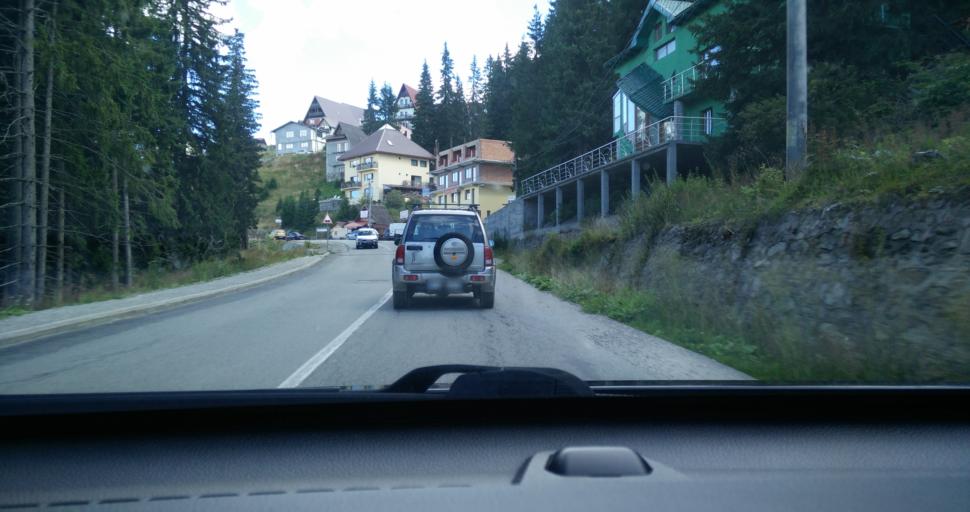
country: RO
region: Gorj
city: Novaci-Straini
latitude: 45.2861
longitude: 23.6921
